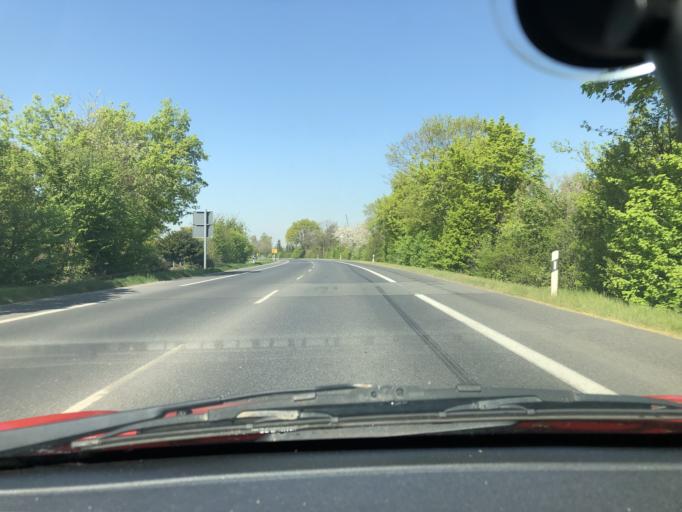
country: DE
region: North Rhine-Westphalia
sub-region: Regierungsbezirk Dusseldorf
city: Kamp-Lintfort
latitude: 51.5018
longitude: 6.5698
